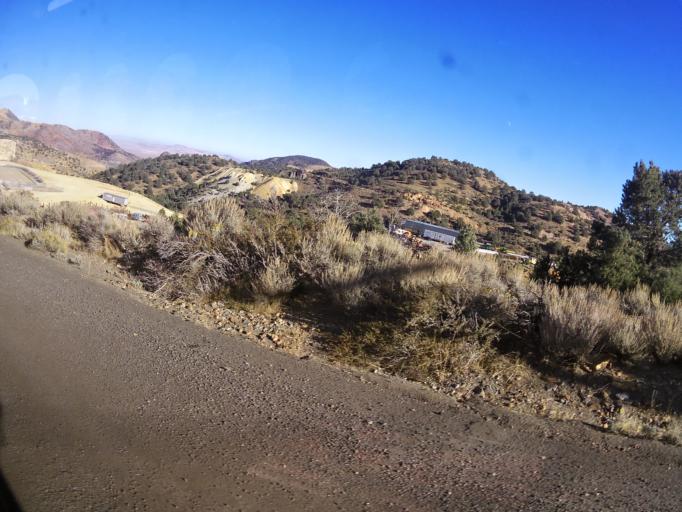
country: US
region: Nevada
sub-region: Storey County
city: Virginia City
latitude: 39.3022
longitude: -119.6511
